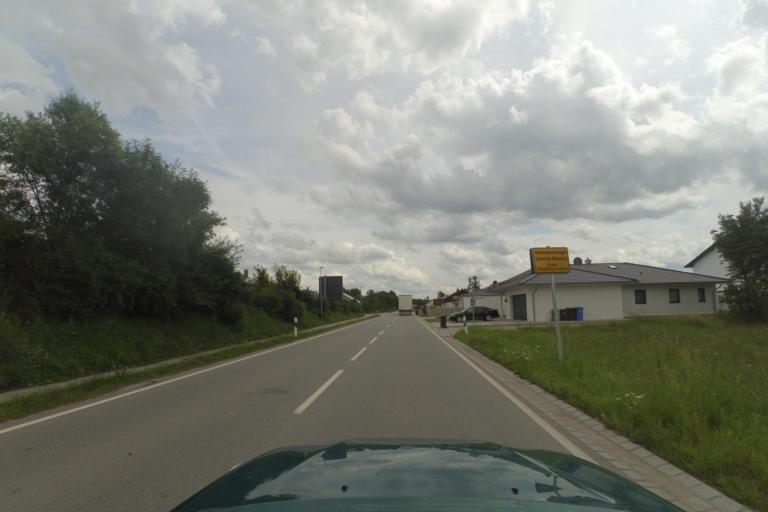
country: DE
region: Bavaria
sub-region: Lower Bavaria
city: Mamming
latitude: 48.6674
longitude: 12.5899
